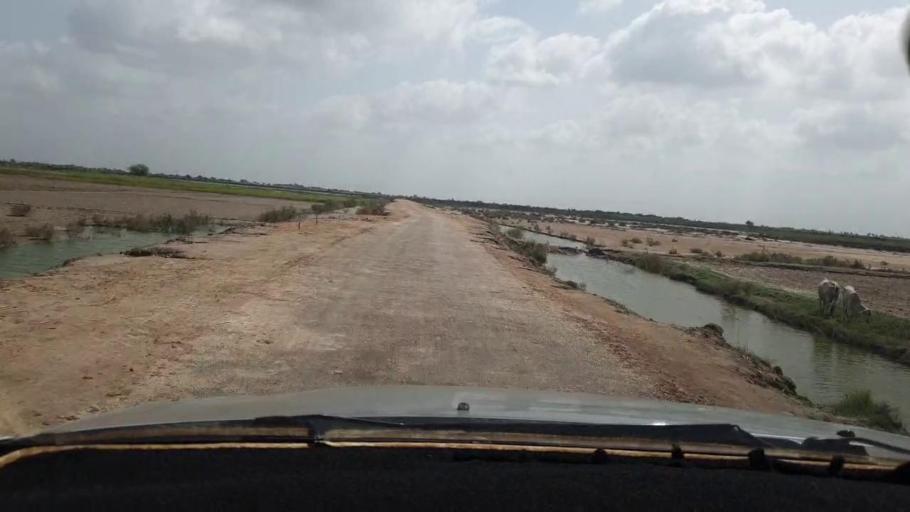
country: PK
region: Sindh
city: Tando Bago
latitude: 24.7207
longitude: 69.1495
